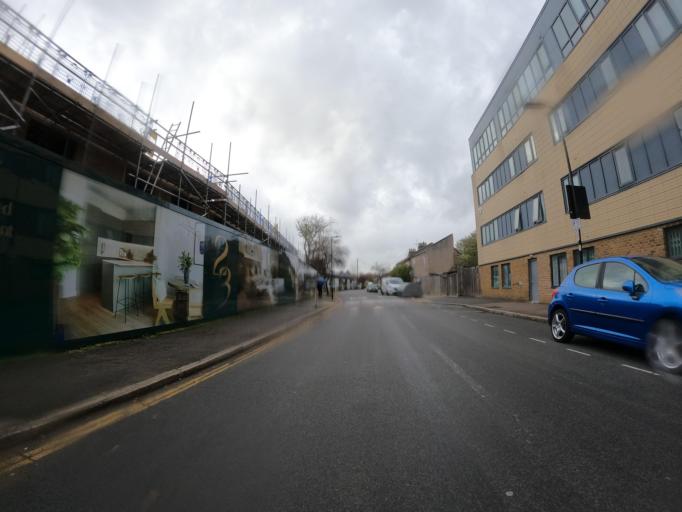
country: GB
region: England
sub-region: Greater London
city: Ealing
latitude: 51.5127
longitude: -0.3236
